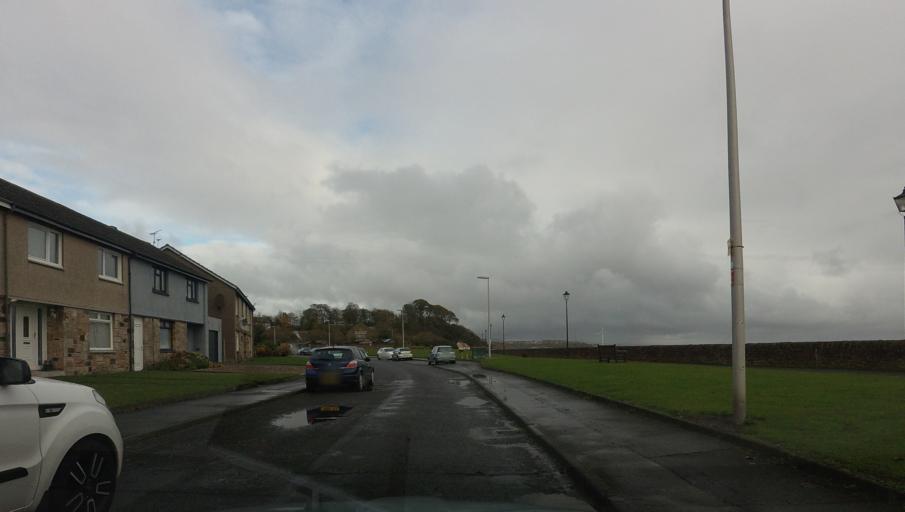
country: GB
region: Scotland
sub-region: Fife
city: East Wemyss
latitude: 56.1576
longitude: -3.0651
